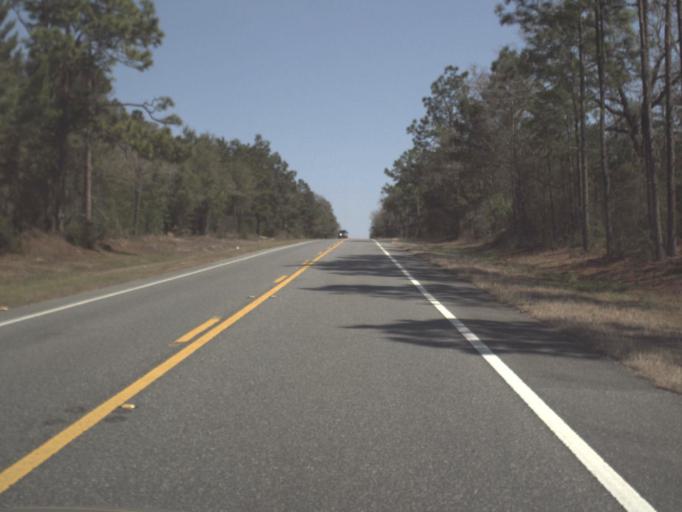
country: US
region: Florida
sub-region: Gadsden County
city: Gretna
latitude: 30.5238
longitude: -84.8045
